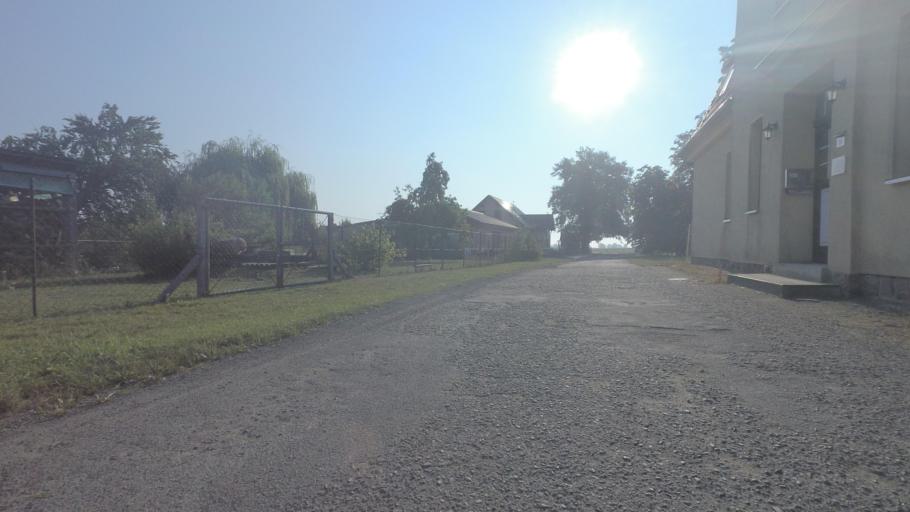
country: DE
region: Brandenburg
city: Heiligengrabe
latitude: 53.2797
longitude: 12.3509
